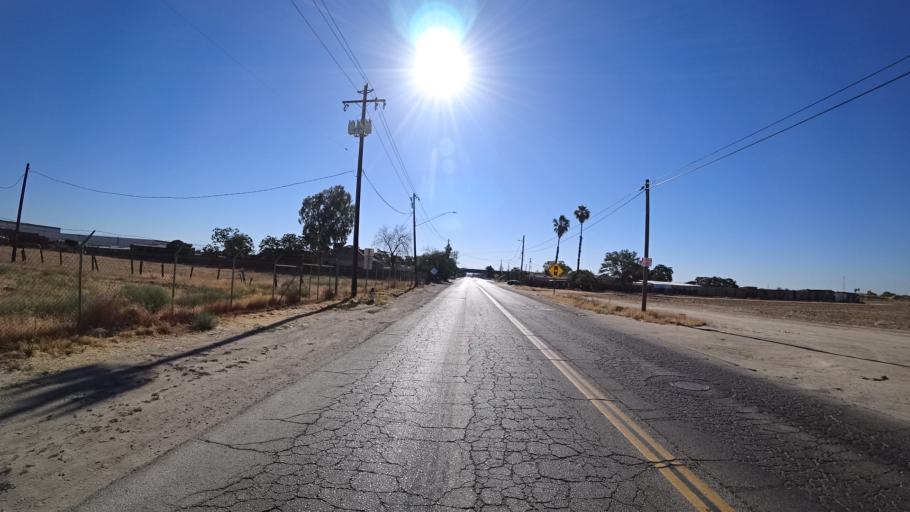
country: US
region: California
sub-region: Fresno County
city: Easton
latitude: 36.6923
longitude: -119.7896
